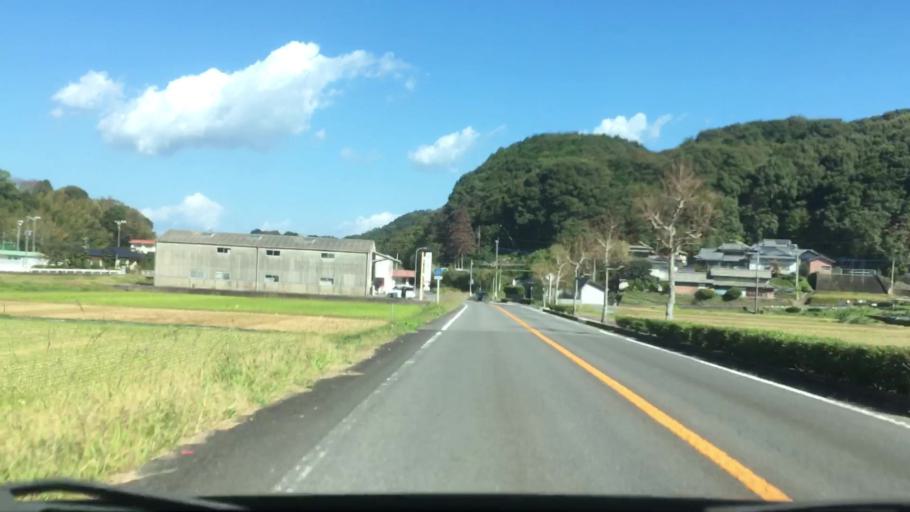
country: JP
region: Nagasaki
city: Sasebo
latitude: 32.9653
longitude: 129.6459
